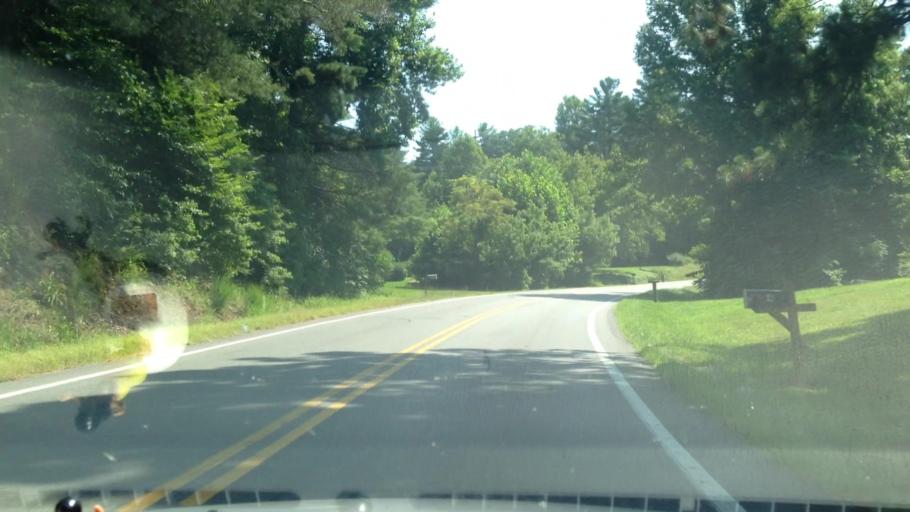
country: US
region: Virginia
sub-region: Patrick County
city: Stuart
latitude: 36.5778
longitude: -80.3724
